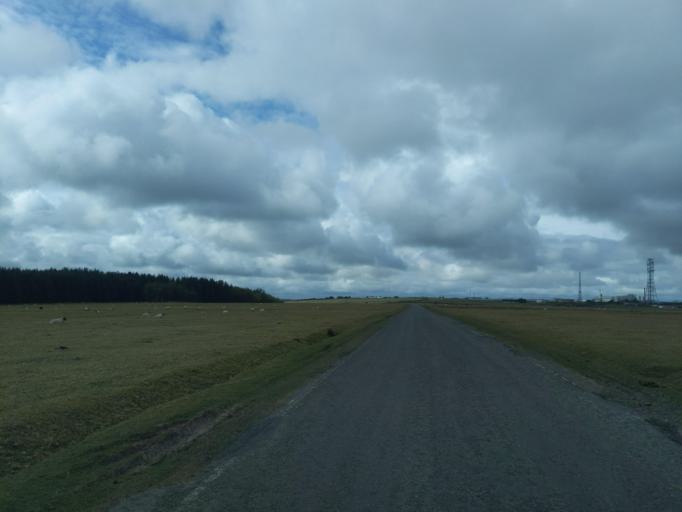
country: GB
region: England
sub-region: Cornwall
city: Camelford
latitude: 50.6372
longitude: -4.6216
